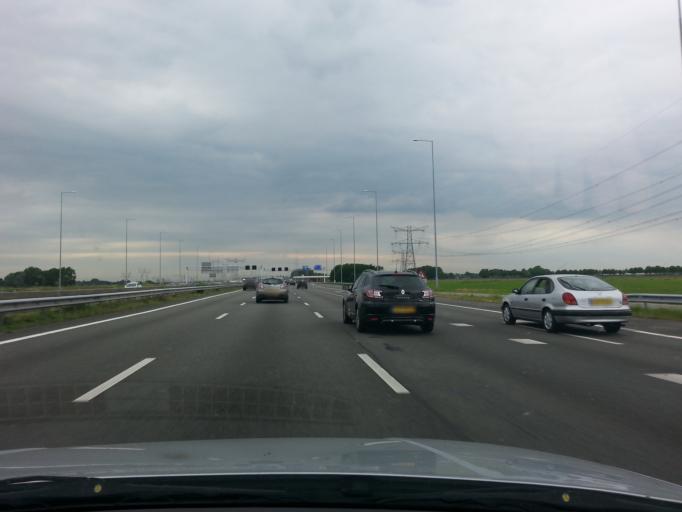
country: NL
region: North Holland
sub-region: Gemeente Weesp
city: Weesp
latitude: 52.3195
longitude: 5.0915
